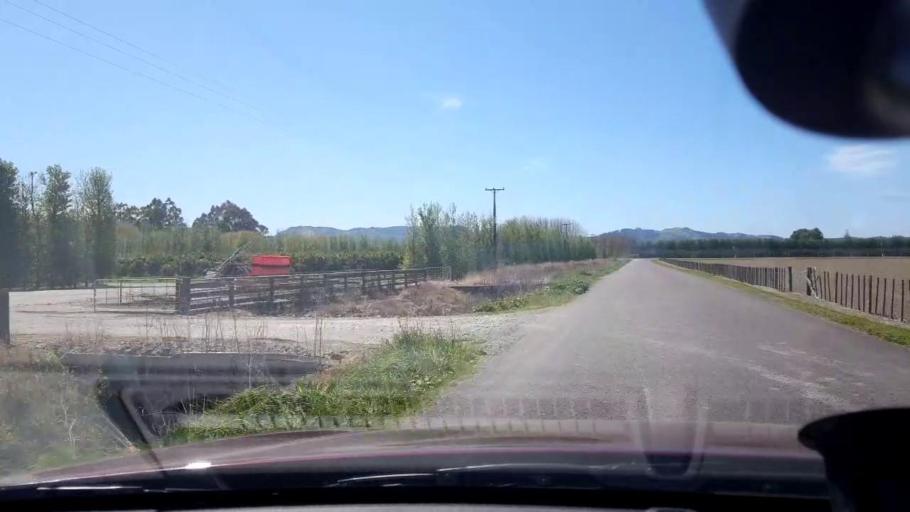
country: NZ
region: Gisborne
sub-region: Gisborne District
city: Gisborne
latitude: -38.6362
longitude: 177.9435
